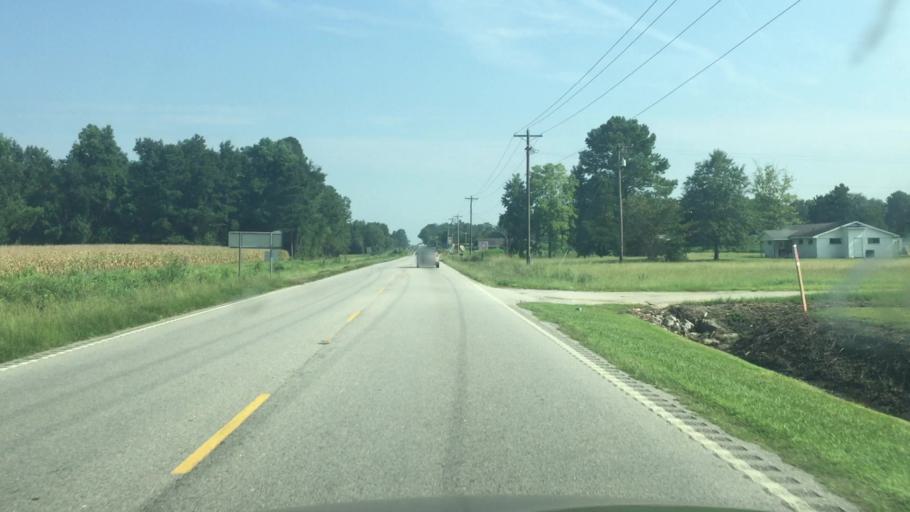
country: US
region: North Carolina
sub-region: Columbus County
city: Tabor City
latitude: 34.1281
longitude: -78.8760
